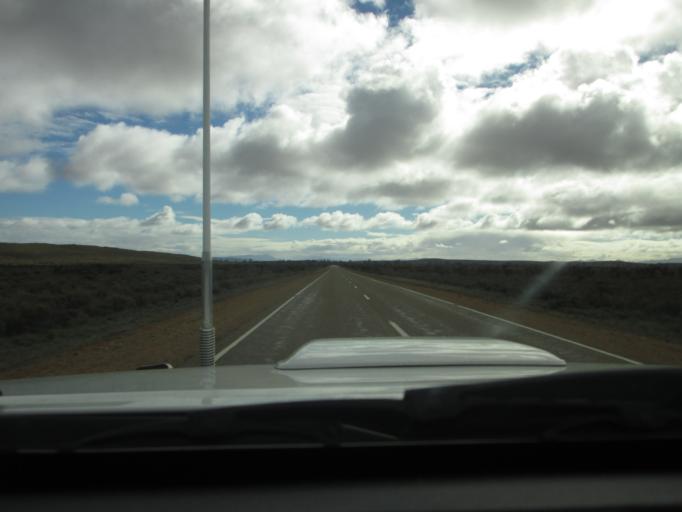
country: AU
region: South Australia
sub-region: Flinders Ranges
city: Quorn
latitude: -32.0943
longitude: 138.5026
